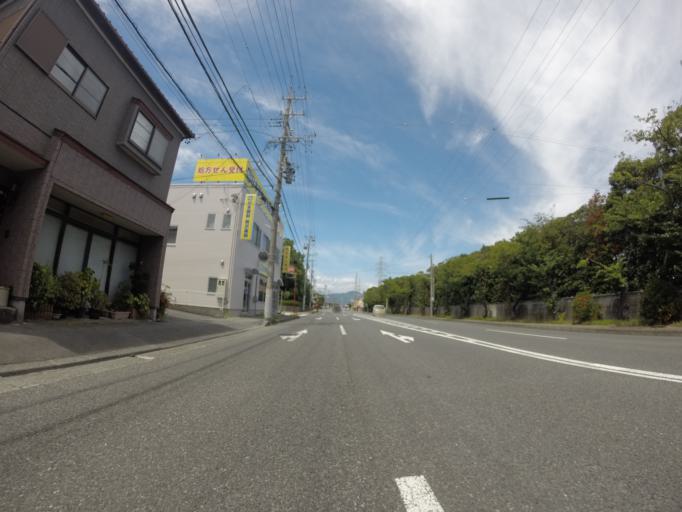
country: JP
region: Shizuoka
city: Shizuoka-shi
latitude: 34.9820
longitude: 138.4917
